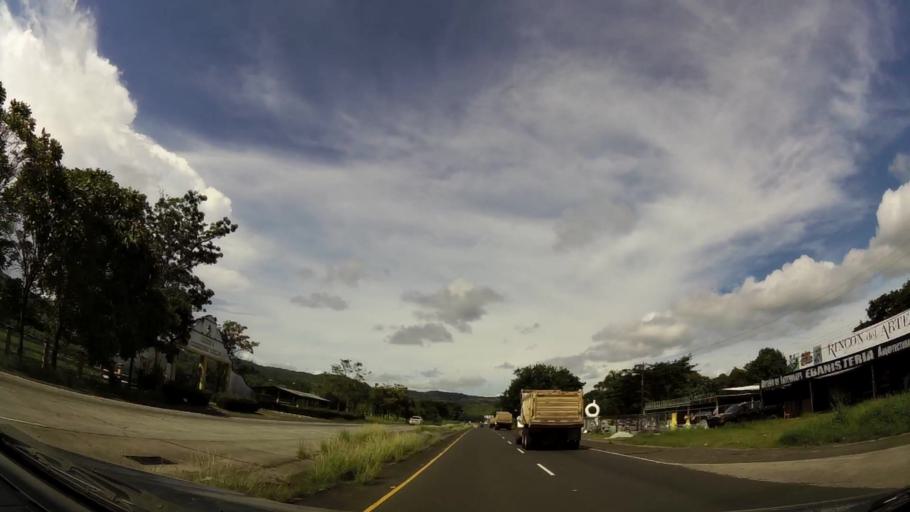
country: PA
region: Panama
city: Capira
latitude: 8.6937
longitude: -79.8675
